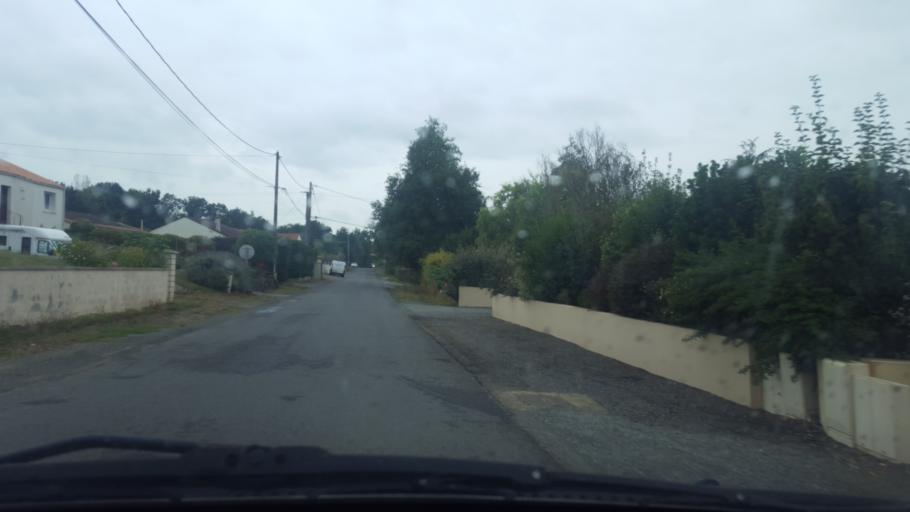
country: FR
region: Pays de la Loire
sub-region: Departement de la Loire-Atlantique
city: Saint-Lumine-de-Coutais
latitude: 47.0541
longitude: -1.7150
